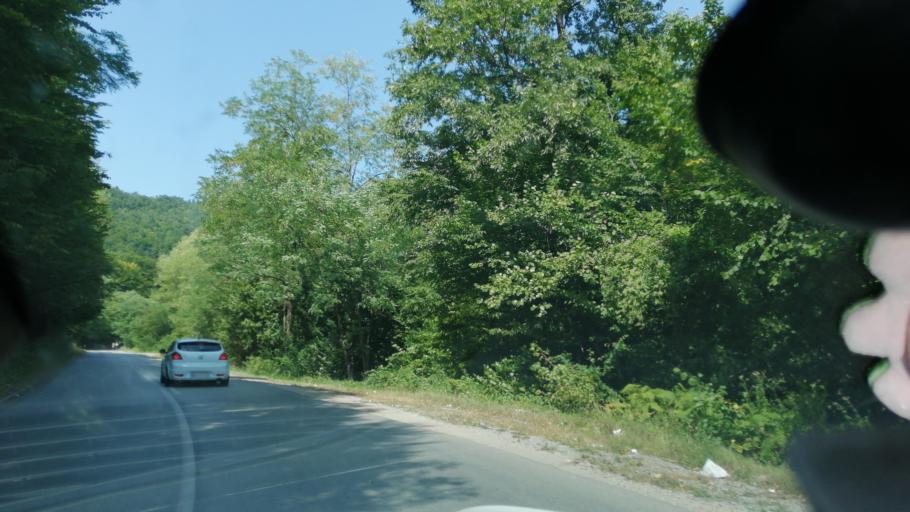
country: RS
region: Central Serbia
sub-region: Moravicki Okrug
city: Ivanjica
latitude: 43.6166
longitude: 20.2367
